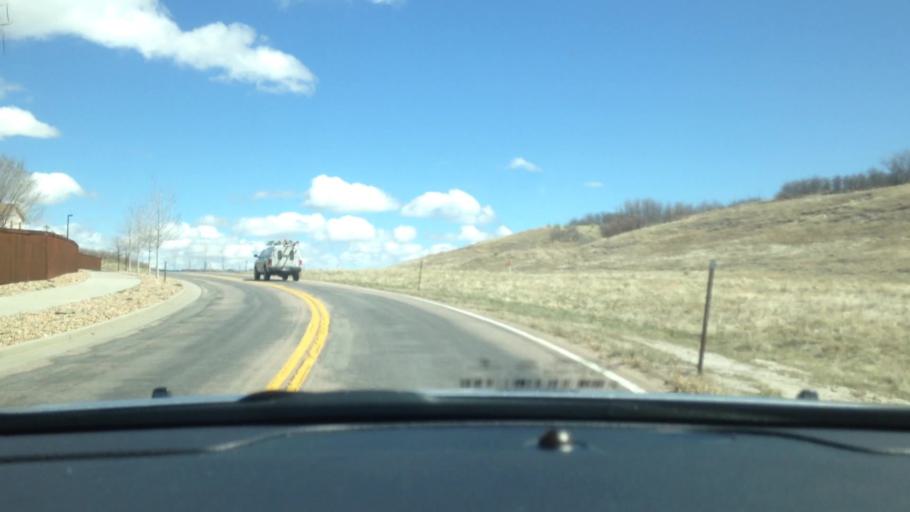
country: US
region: Colorado
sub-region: Douglas County
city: Castle Rock
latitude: 39.3744
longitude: -104.8817
